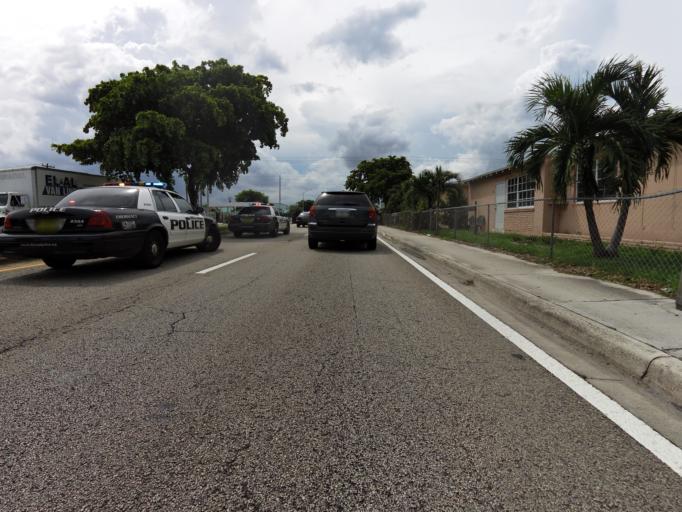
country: US
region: Florida
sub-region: Broward County
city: Dania Beach
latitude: 26.0336
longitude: -80.1469
